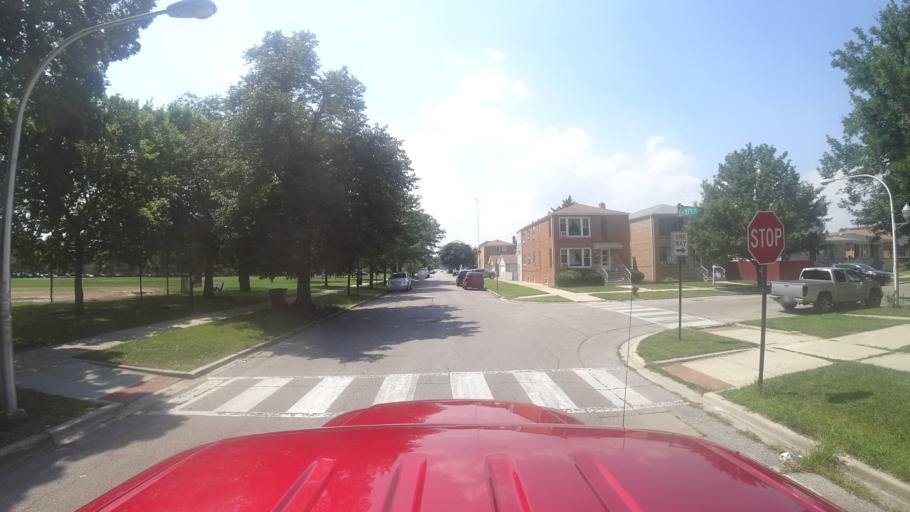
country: US
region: Illinois
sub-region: Cook County
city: Hometown
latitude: 41.7894
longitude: -87.7314
